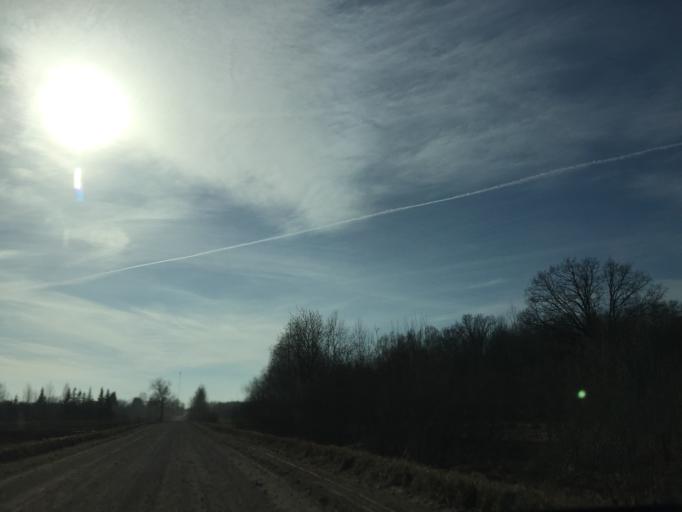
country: LV
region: Saulkrastu
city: Saulkrasti
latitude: 57.2939
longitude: 24.5299
